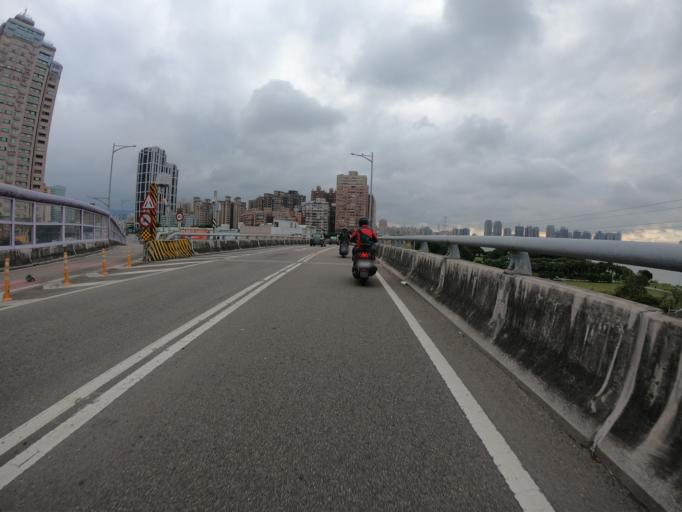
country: TW
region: Taipei
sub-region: Taipei
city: Banqiao
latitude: 25.0143
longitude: 121.5053
